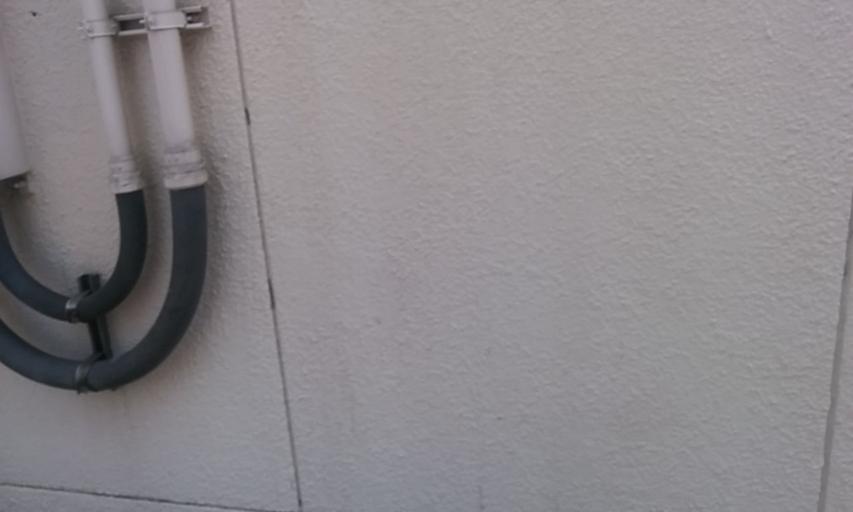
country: JP
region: Tokyo
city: Urayasu
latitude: 35.7025
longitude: 139.8481
